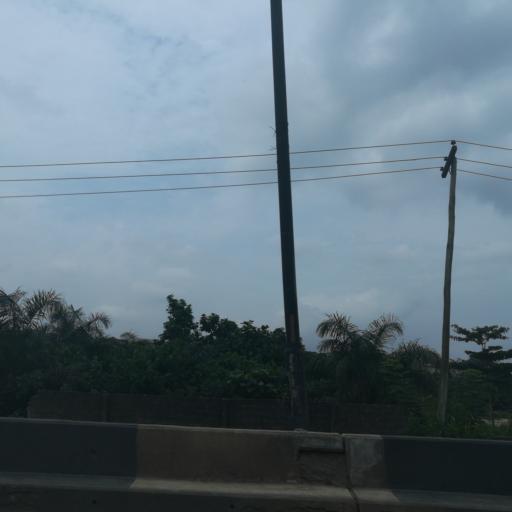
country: NG
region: Lagos
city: Ojota
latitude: 6.5785
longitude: 3.3953
